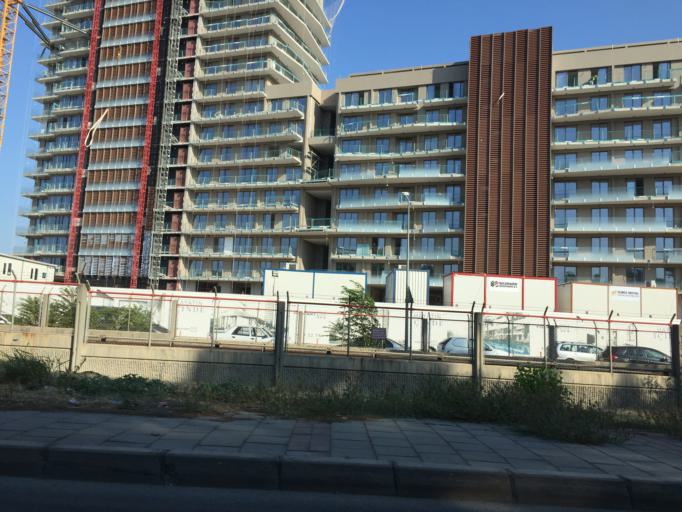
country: TR
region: Izmir
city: Buca
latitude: 38.4460
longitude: 27.1869
